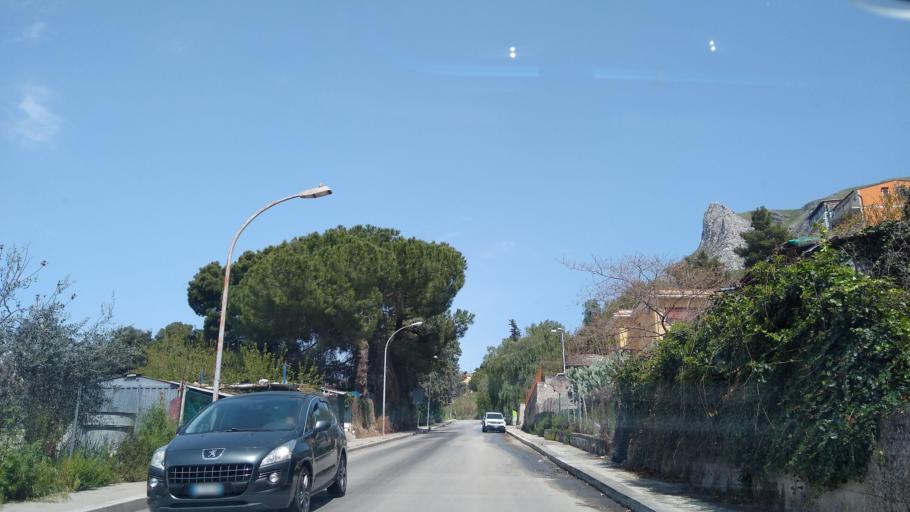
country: IT
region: Sicily
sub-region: Palermo
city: San Cipirello
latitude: 37.9654
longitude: 13.1770
